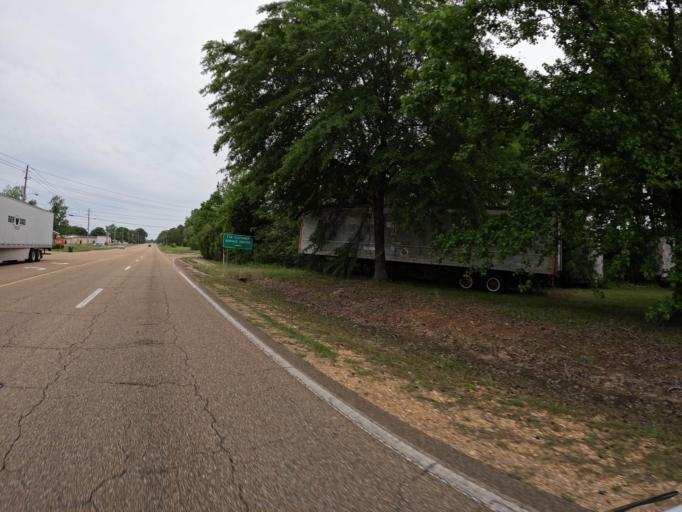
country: US
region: Mississippi
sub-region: Lee County
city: Tupelo
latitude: 34.2924
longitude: -88.7549
